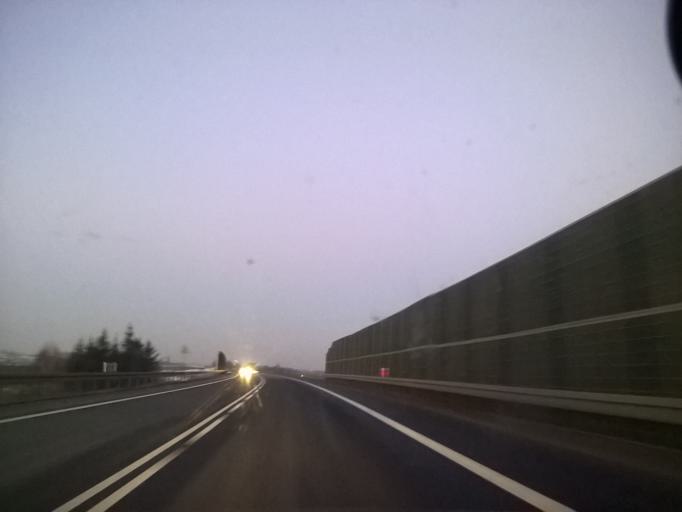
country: PL
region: Warmian-Masurian Voivodeship
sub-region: Powiat olsztynski
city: Biskupiec
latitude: 53.8360
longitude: 20.9268
